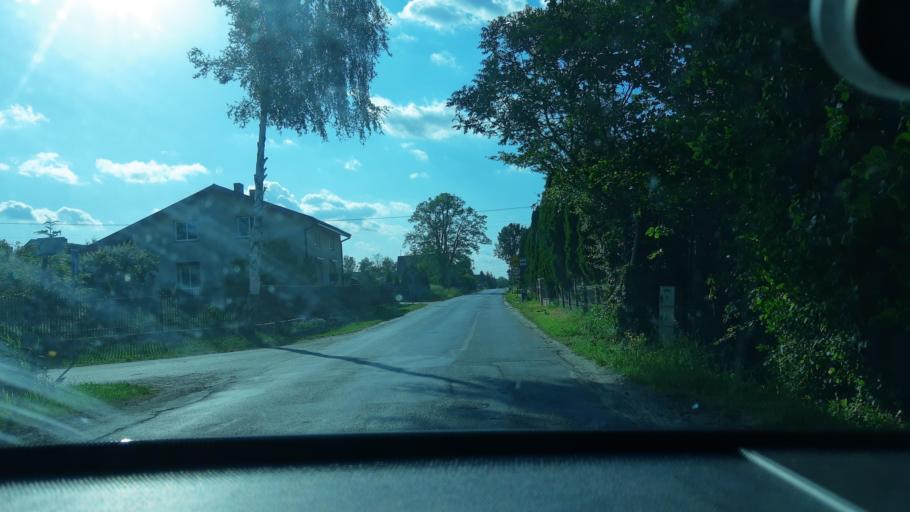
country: PL
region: Lodz Voivodeship
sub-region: Powiat sieradzki
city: Sieradz
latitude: 51.5462
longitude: 18.7813
